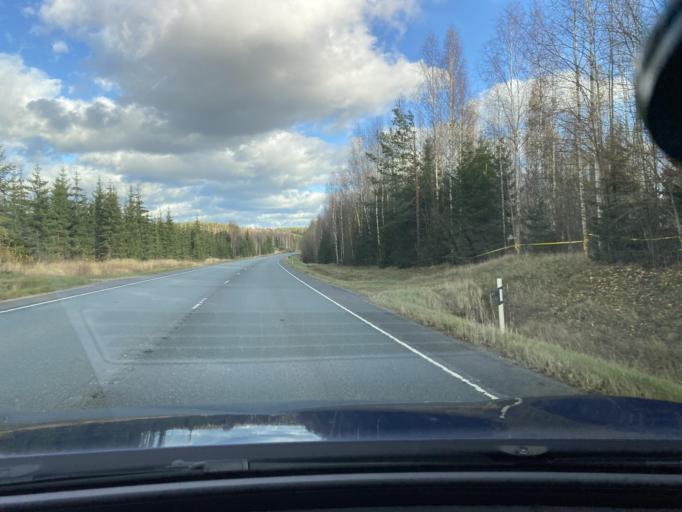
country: FI
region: Haeme
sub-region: Riihimaeki
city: Riihimaeki
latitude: 60.7786
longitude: 24.8452
